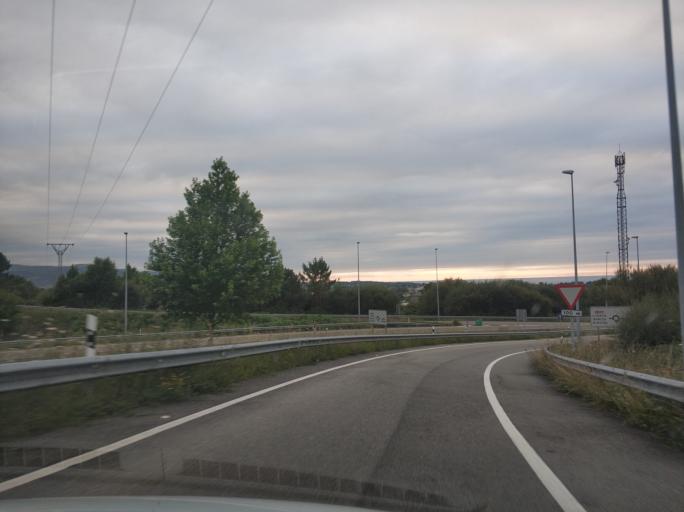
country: ES
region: Asturias
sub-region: Province of Asturias
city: Tineo
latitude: 43.5350
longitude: -6.5020
